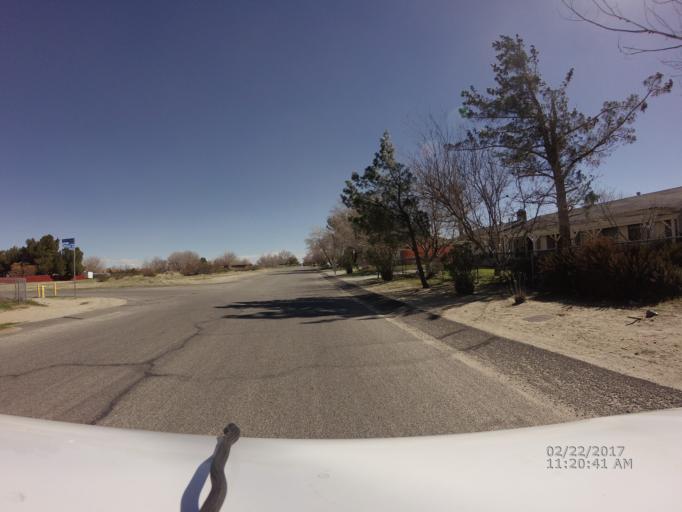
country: US
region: California
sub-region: Los Angeles County
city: Lake Los Angeles
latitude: 34.6175
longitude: -117.8129
